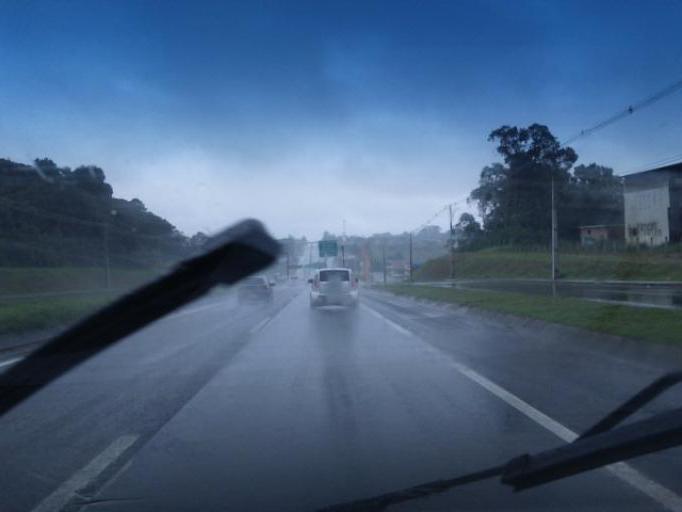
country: BR
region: Parana
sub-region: Sao Jose Dos Pinhais
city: Sao Jose dos Pinhais
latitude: -25.5800
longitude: -49.1780
